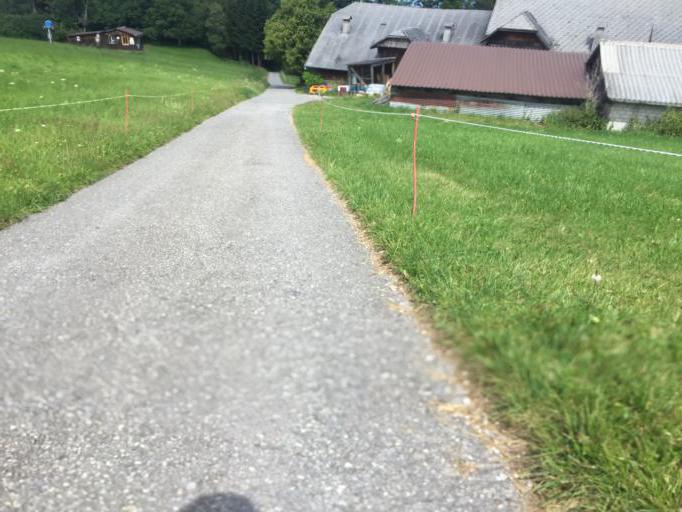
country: CH
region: Bern
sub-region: Thun District
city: Burgistein
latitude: 46.7580
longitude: 7.4475
